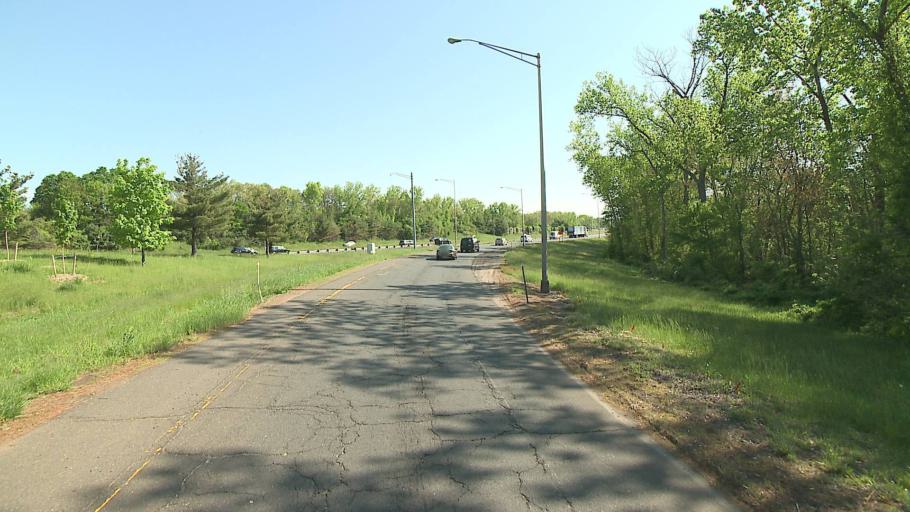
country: US
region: Connecticut
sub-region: Hartford County
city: Manchester
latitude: 41.8120
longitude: -72.5169
